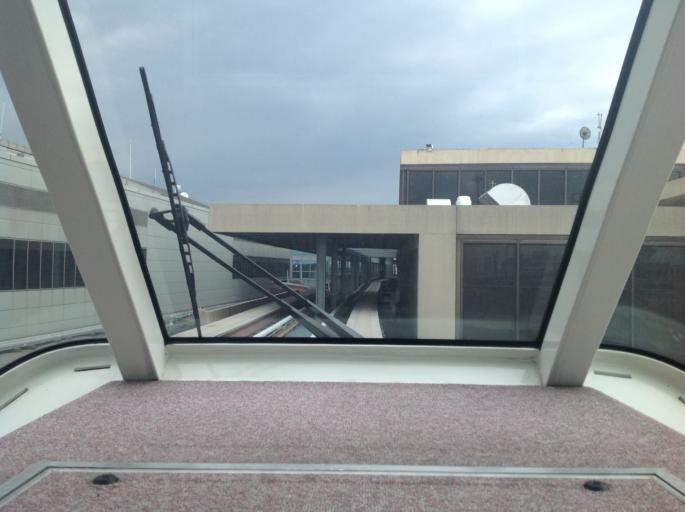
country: US
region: New Jersey
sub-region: Essex County
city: Newark
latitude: 40.6917
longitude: -74.1763
